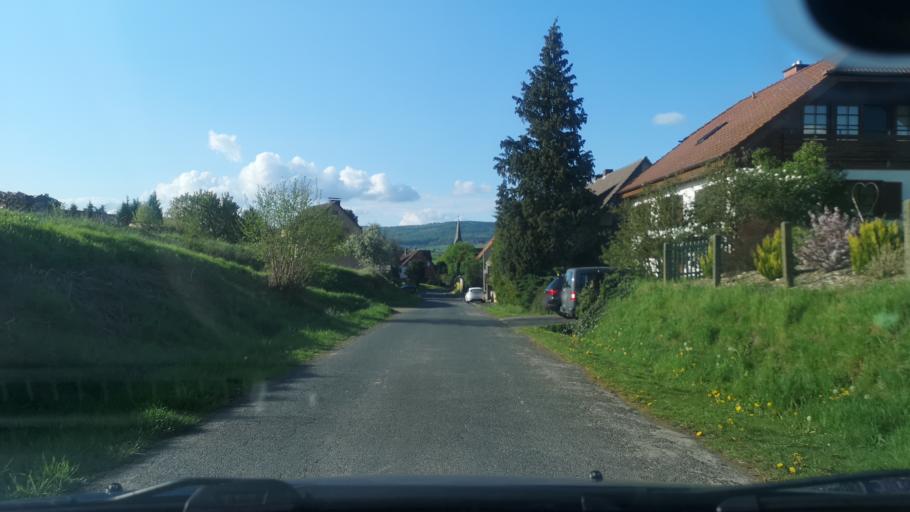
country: DE
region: Lower Saxony
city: Uslar
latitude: 51.6507
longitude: 9.6808
